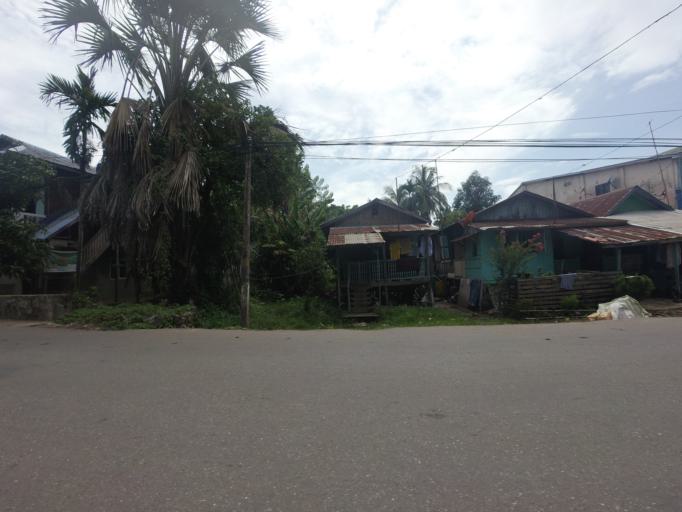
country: MM
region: Mon
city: Mawlamyine
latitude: 16.4537
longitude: 97.6273
